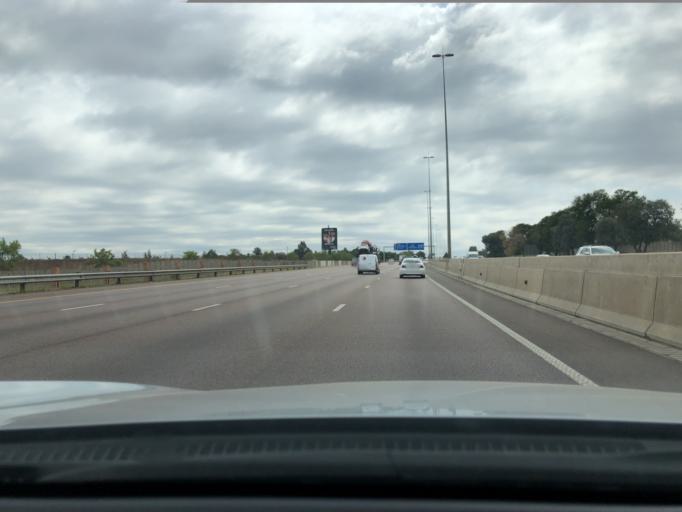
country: ZA
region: Gauteng
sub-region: City of Tshwane Metropolitan Municipality
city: Centurion
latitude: -25.8402
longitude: 28.2331
